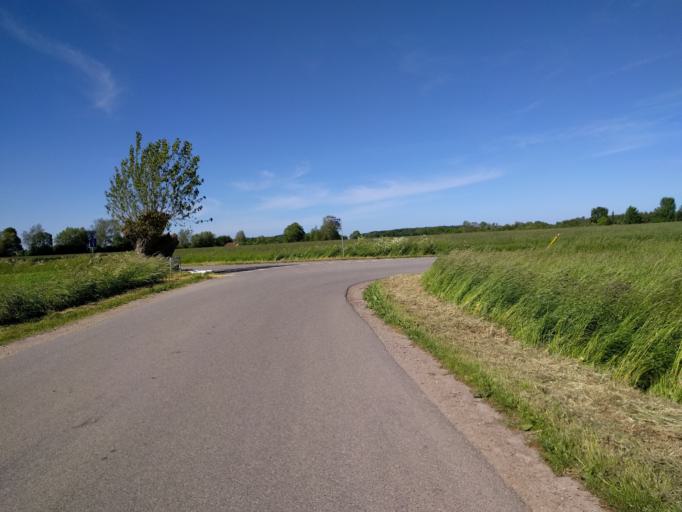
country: DK
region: South Denmark
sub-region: Kerteminde Kommune
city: Kerteminde
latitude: 55.4220
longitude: 10.6607
